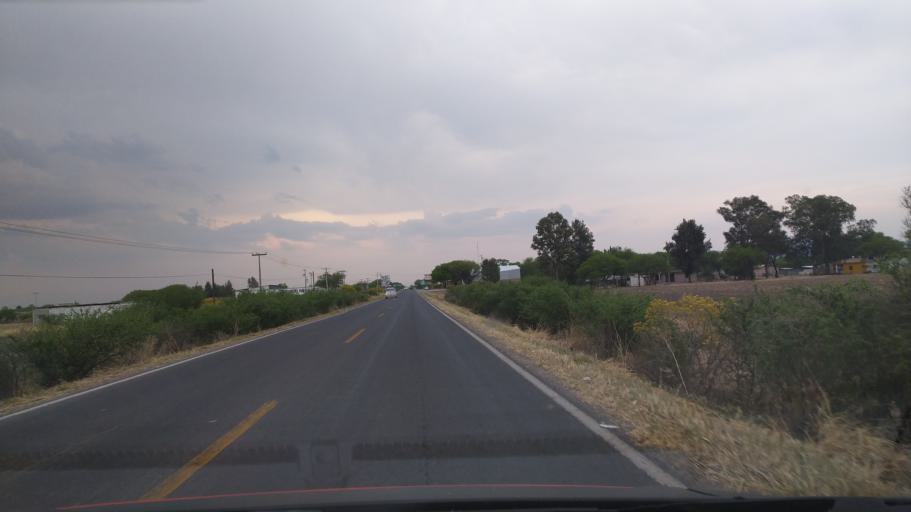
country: MX
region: Guanajuato
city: Ciudad Manuel Doblado
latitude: 20.7486
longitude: -101.9257
